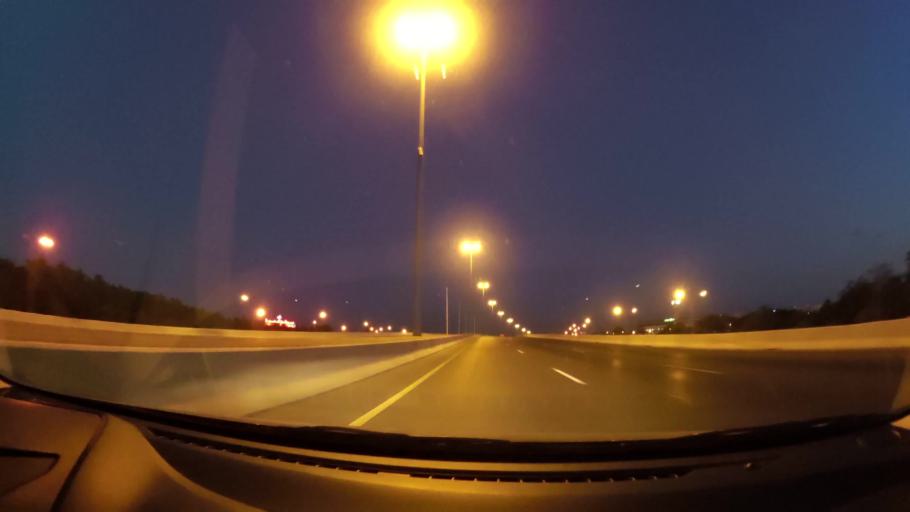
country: OM
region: Muhafazat Masqat
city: As Sib al Jadidah
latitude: 23.6154
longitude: 58.2437
